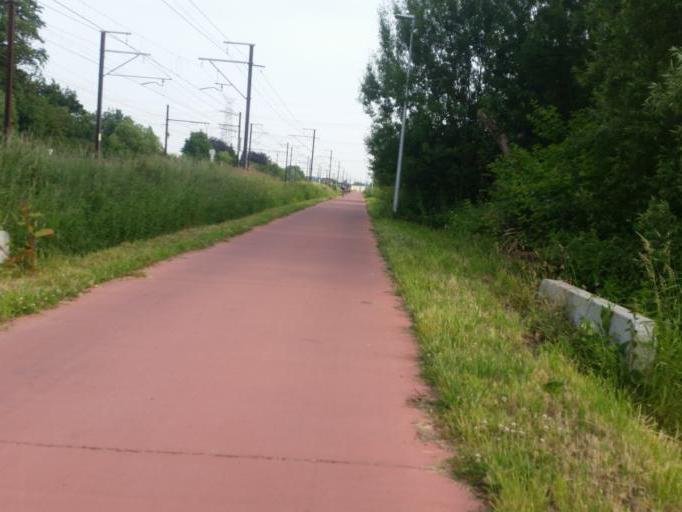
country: BE
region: Flanders
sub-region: Provincie Antwerpen
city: Lint
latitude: 51.1209
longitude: 4.4836
